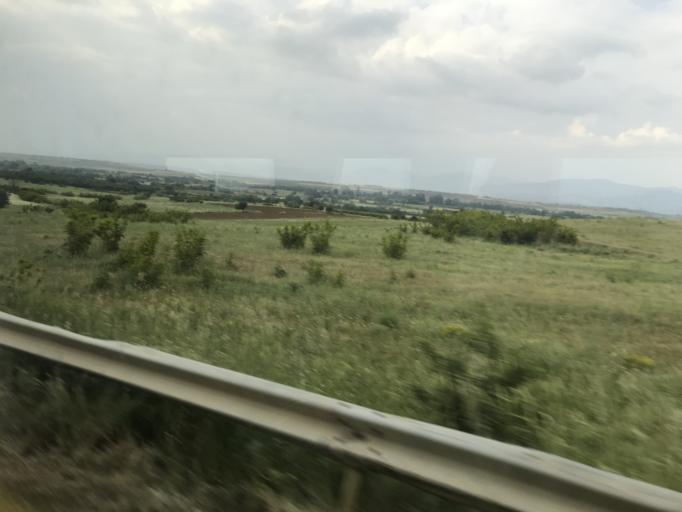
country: GR
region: East Macedonia and Thrace
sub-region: Nomos Rodopis
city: Sapes
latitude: 41.0301
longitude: 25.6845
